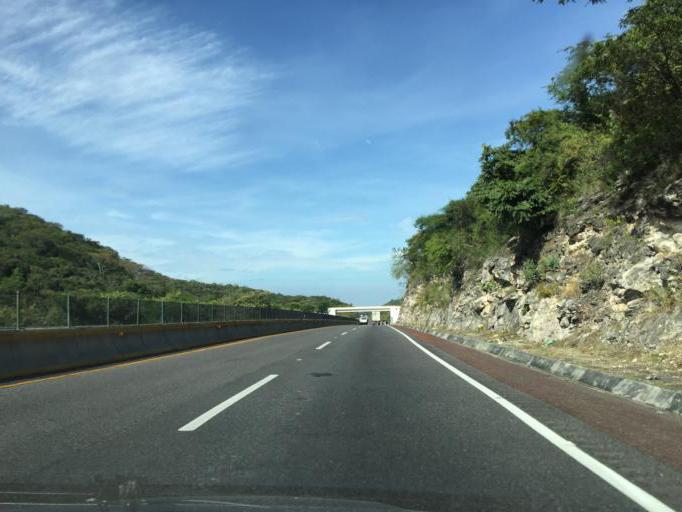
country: MX
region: Guerrero
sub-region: Huitzuco de los Figueroa
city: Ciudad de Huitzuco
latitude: 18.2854
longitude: -99.2095
